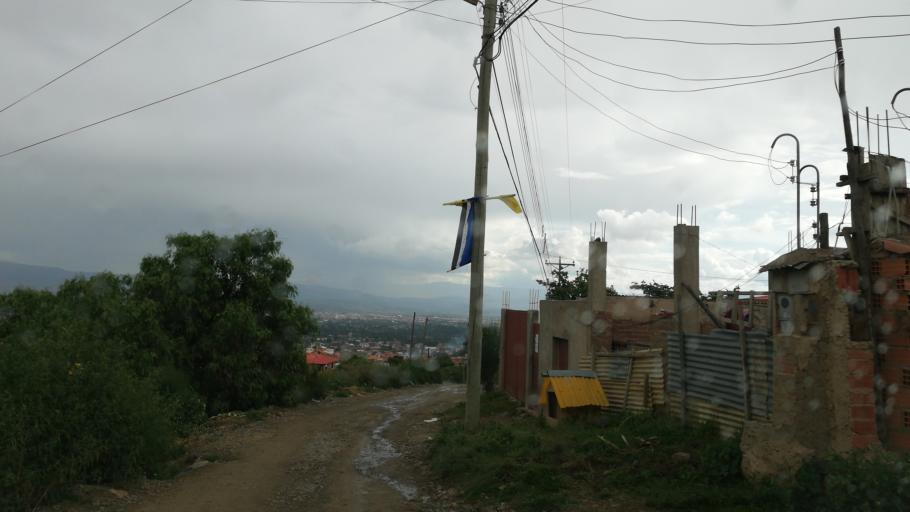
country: BO
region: Cochabamba
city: Cochabamba
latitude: -17.3295
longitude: -66.1930
